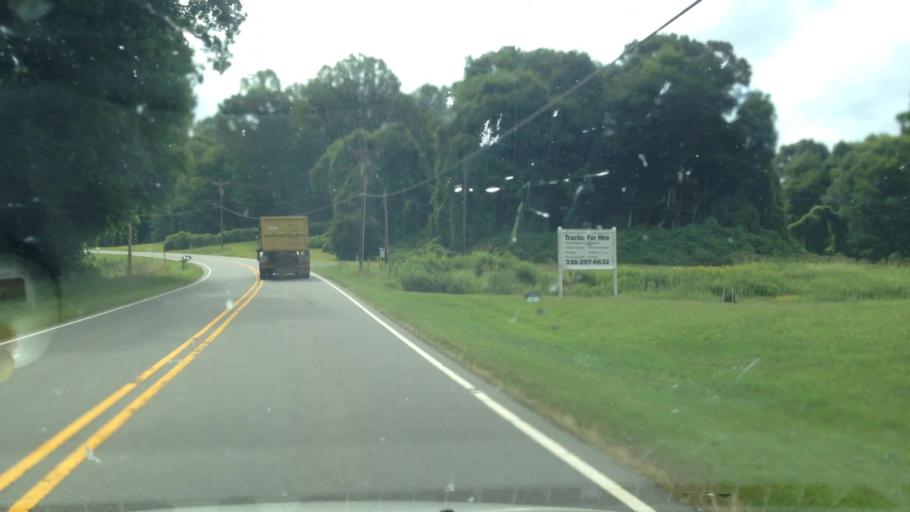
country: US
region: North Carolina
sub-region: Rockingham County
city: Wentworth
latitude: 36.3973
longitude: -79.7660
